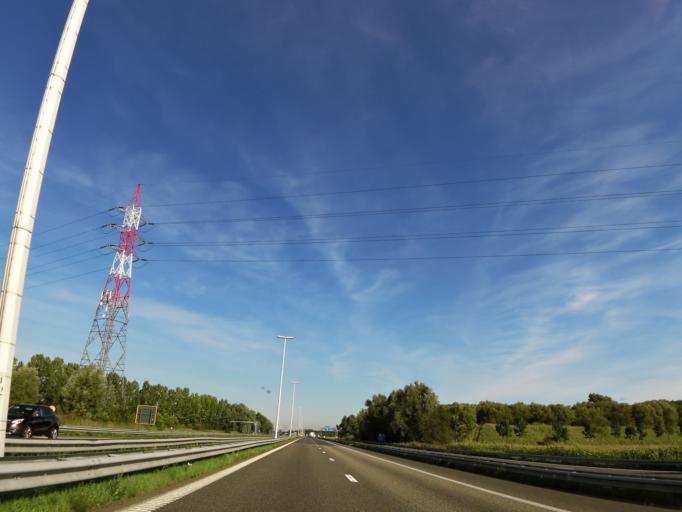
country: NL
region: North Brabant
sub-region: Gemeente Woensdrecht
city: Woensdrecht
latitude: 51.3731
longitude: 4.3065
